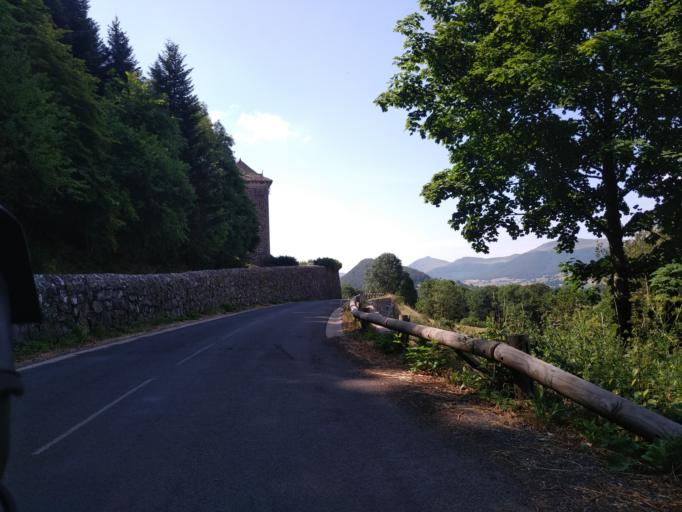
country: FR
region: Auvergne
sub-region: Departement du Cantal
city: Riom-es-Montagnes
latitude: 45.1991
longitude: 2.7175
